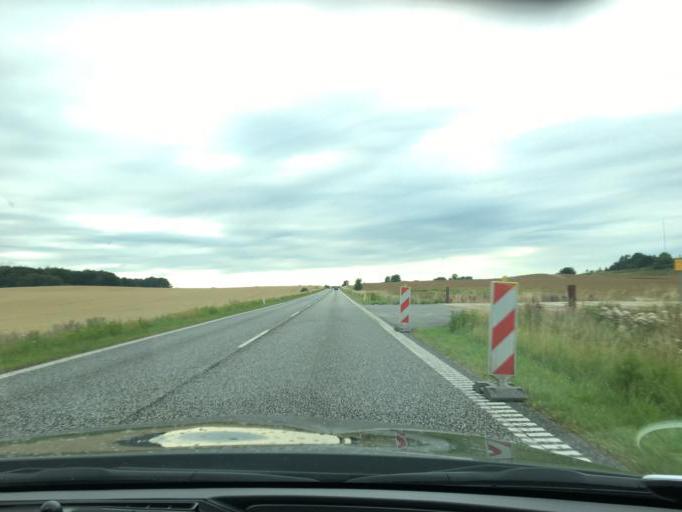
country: DK
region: Capital Region
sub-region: Allerod Kommune
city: Blovstrod
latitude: 55.9014
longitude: 12.4174
